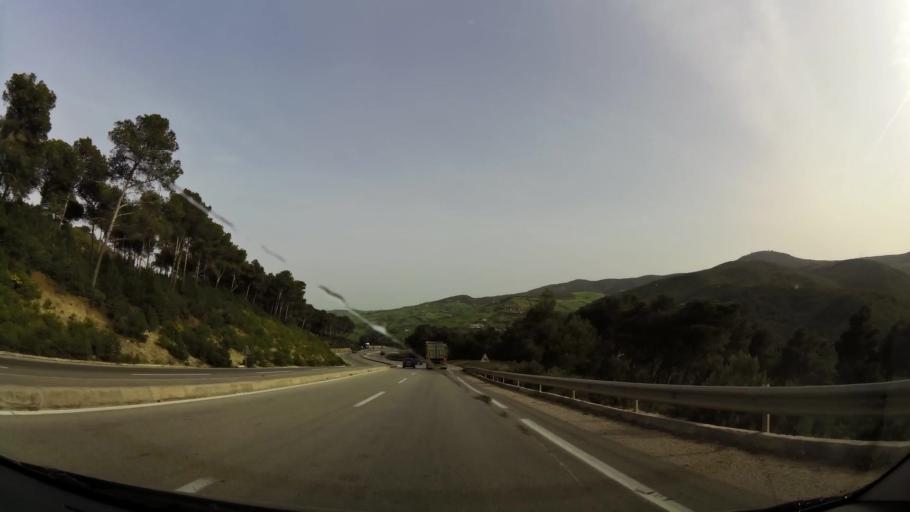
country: MA
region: Tanger-Tetouan
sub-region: Tetouan
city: Saddina
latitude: 35.5494
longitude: -5.5673
